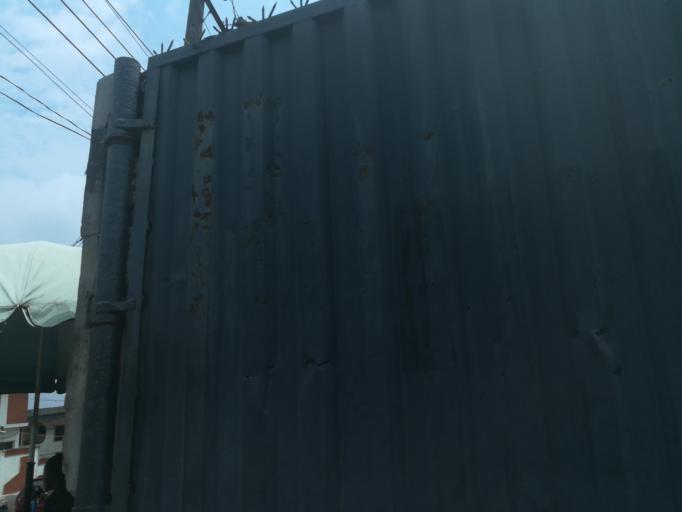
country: NG
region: Lagos
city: Ojota
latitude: 6.5912
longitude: 3.3635
